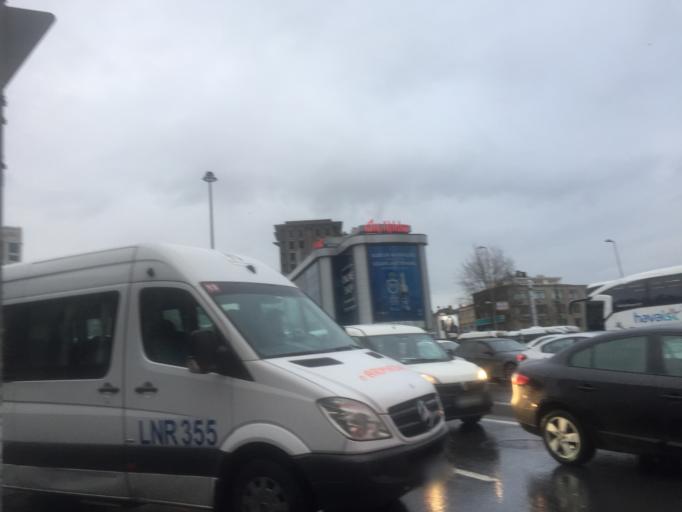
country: TR
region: Istanbul
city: Sisli
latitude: 41.0724
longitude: 29.0159
